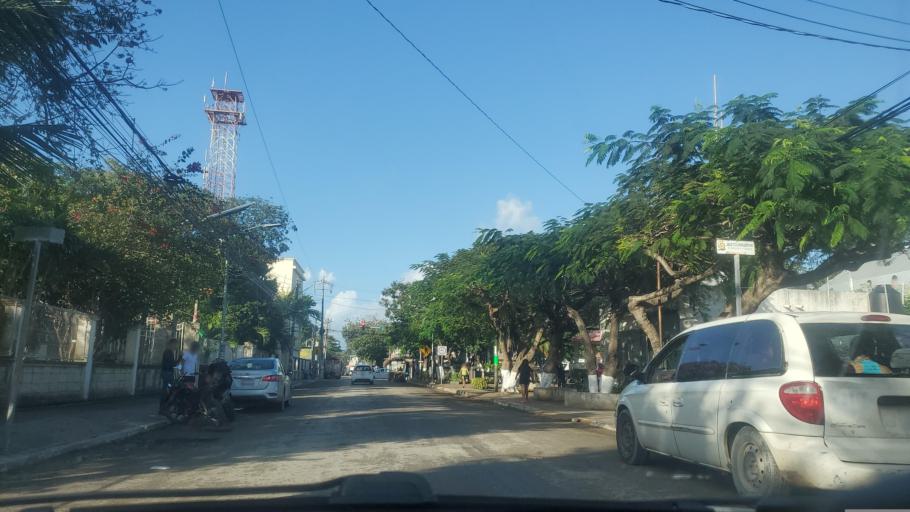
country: MX
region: Quintana Roo
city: Tulum
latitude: 20.2097
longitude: -87.4626
